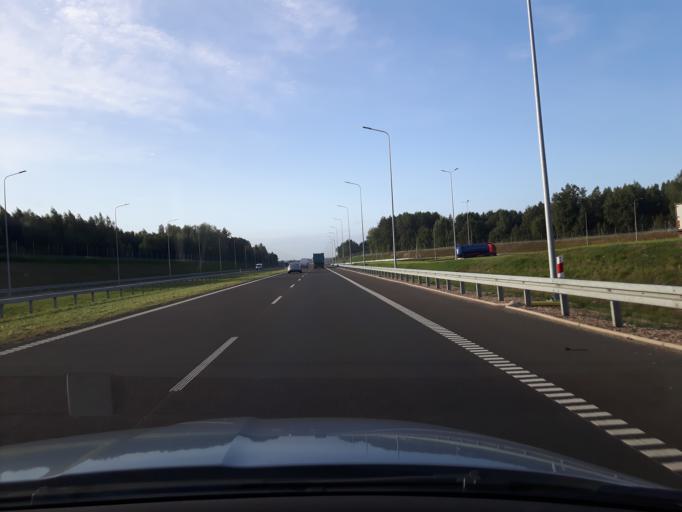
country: PL
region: Masovian Voivodeship
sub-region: Powiat radomski
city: Zakrzew
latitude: 51.4422
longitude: 21.0339
